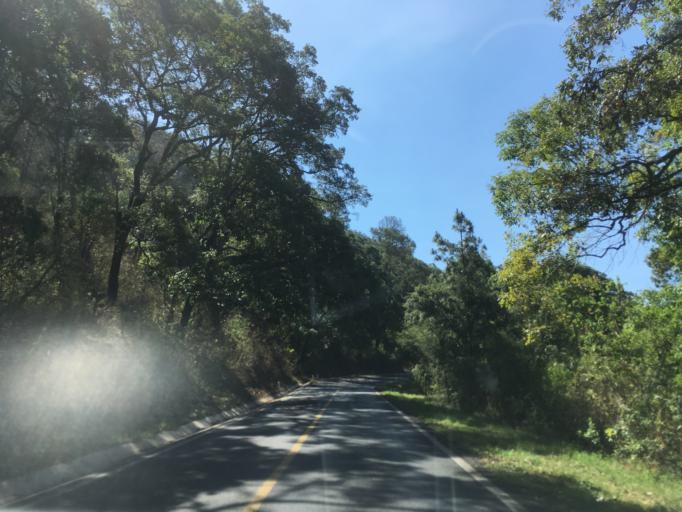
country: MX
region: Michoacan
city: Tzitzio
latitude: 19.6513
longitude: -100.9719
